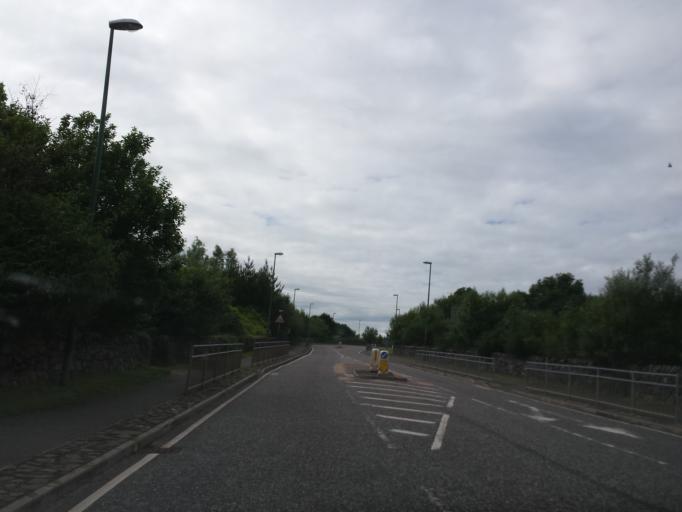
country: GB
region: Scotland
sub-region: Argyll and Bute
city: Isle Of Mull
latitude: 56.9114
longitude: -5.8398
